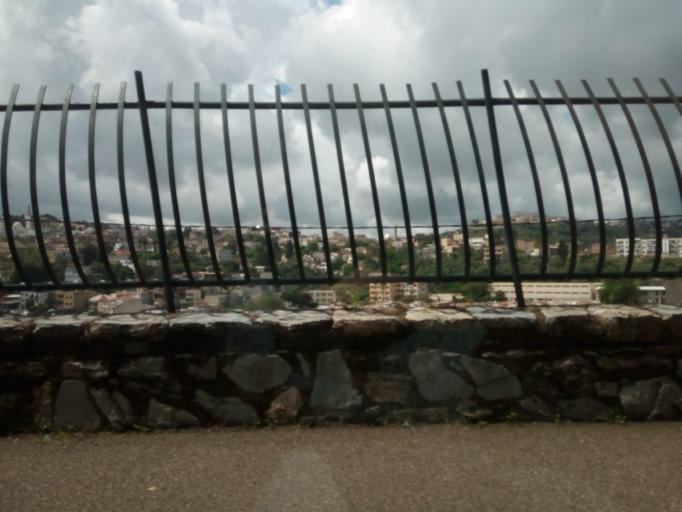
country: DZ
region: Alger
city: Algiers
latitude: 36.7795
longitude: 3.0491
